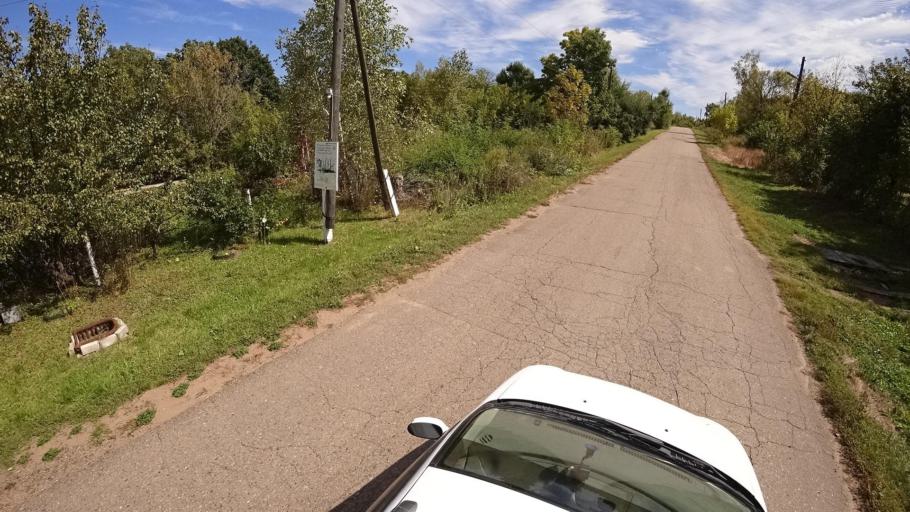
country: RU
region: Primorskiy
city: Yakovlevka
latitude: 44.6580
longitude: 133.7368
